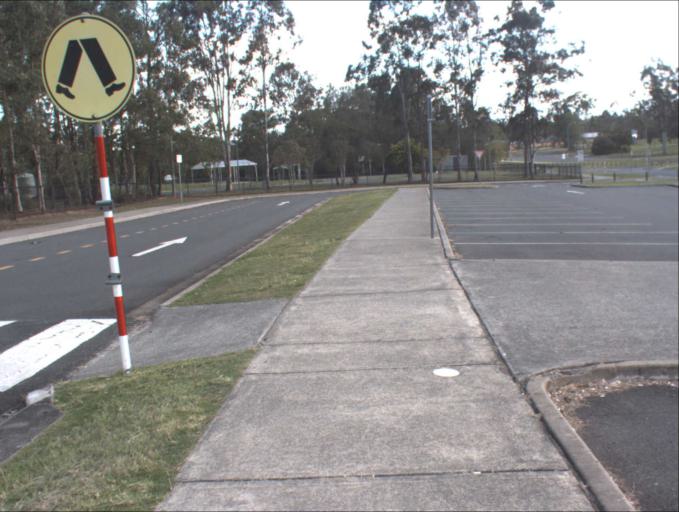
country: AU
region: Queensland
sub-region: Logan
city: North Maclean
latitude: -27.8070
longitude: 152.9572
